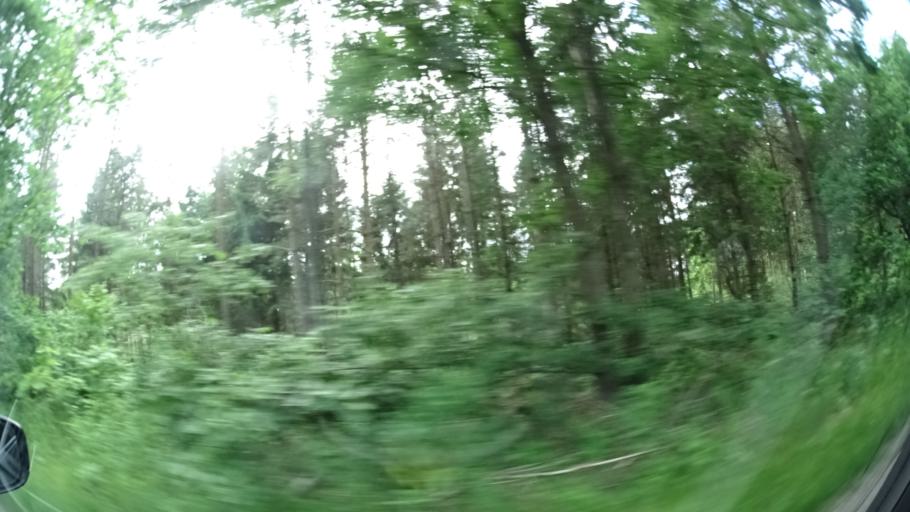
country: DK
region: Central Jutland
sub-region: Syddjurs Kommune
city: Ryomgard
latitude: 56.3629
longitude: 10.4954
